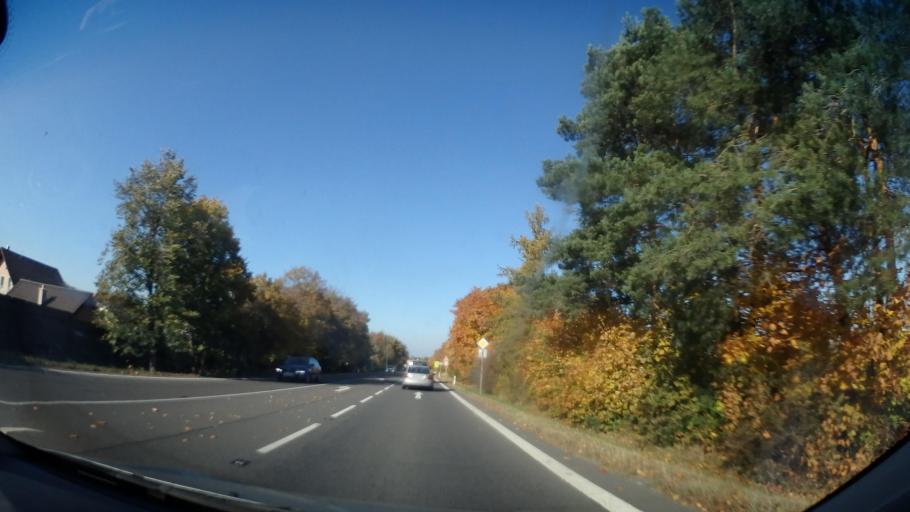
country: CZ
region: Pardubicky
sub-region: Okres Chrudim
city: Slatinany
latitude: 49.9083
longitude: 15.8202
